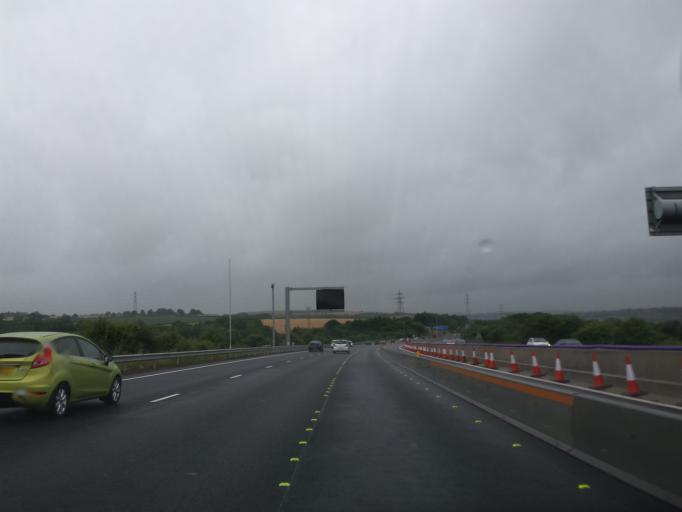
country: GB
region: England
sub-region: Derbyshire
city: Barlborough
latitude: 53.2667
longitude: -1.3059
